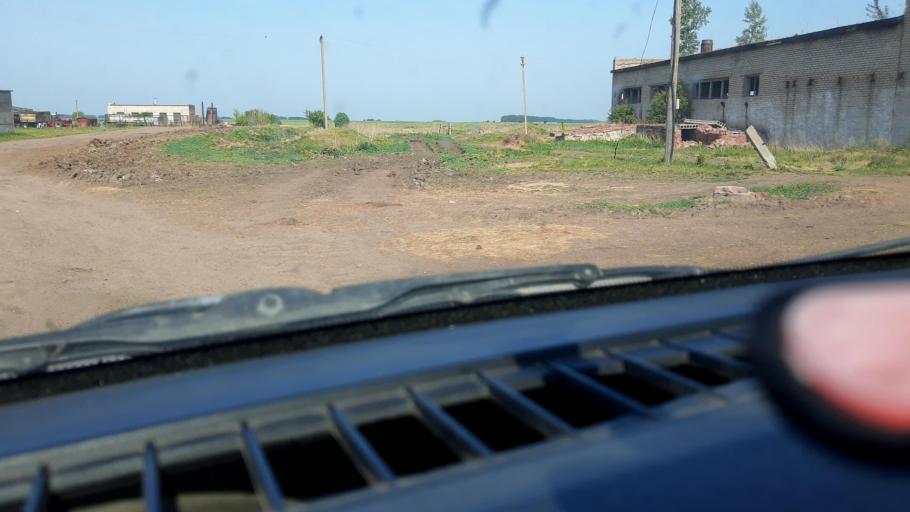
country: RU
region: Bashkortostan
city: Asanovo
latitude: 54.9109
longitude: 55.4950
